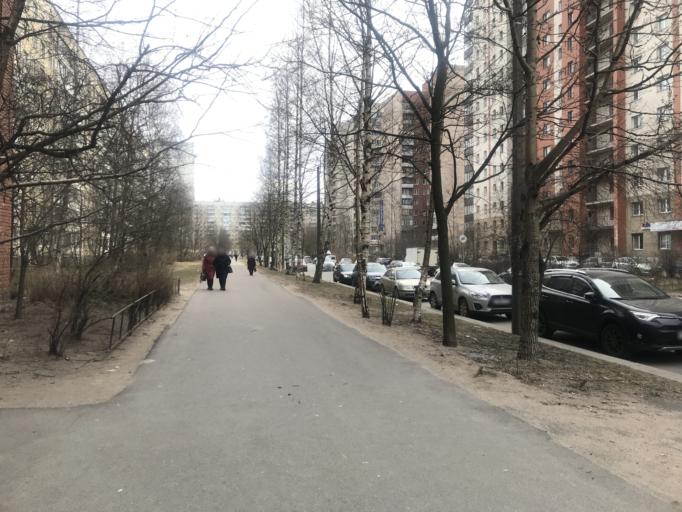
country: RU
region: St.-Petersburg
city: Ozerki
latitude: 60.0484
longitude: 30.3253
